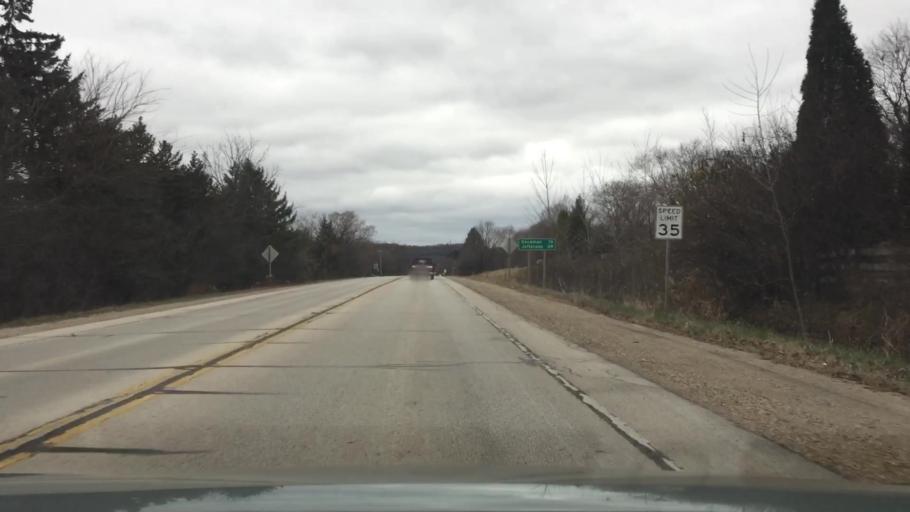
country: US
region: Wisconsin
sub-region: Waukesha County
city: Waukesha
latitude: 43.0212
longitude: -88.2722
